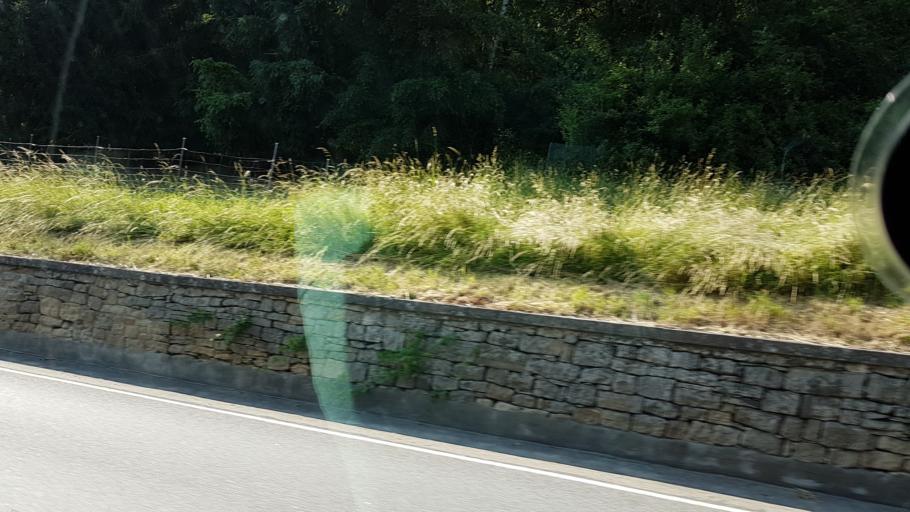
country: DE
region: Rheinland-Pfalz
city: Offenbach-Hundheim
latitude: 49.6202
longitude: 7.5478
